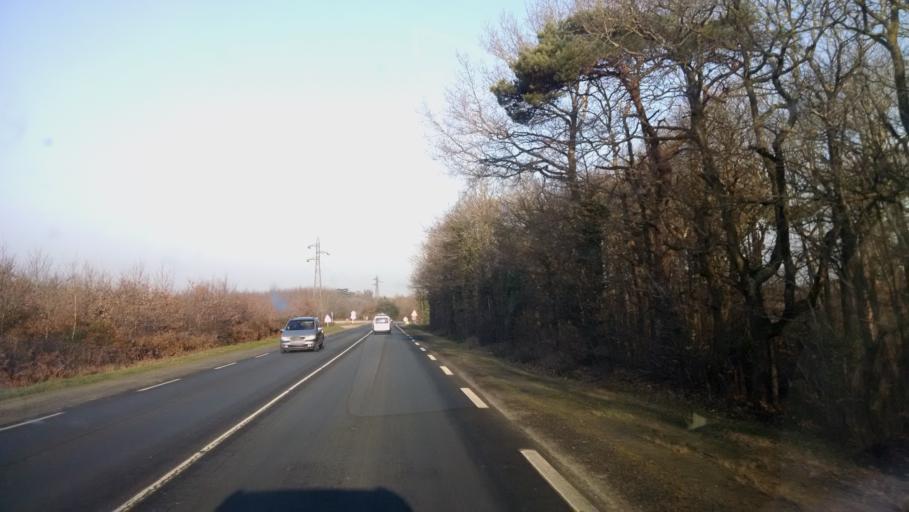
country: FR
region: Pays de la Loire
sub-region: Departement de la Loire-Atlantique
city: Le Bignon
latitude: 47.1282
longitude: -1.5021
